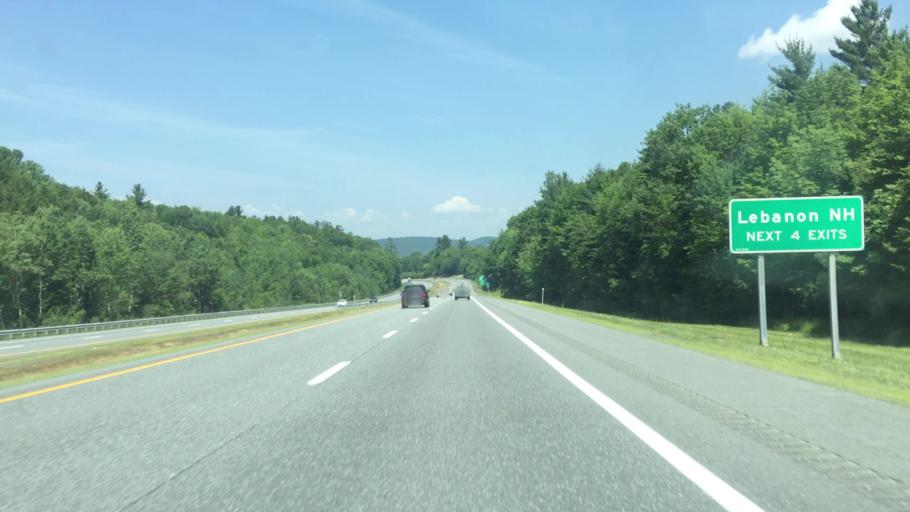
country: US
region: New Hampshire
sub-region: Grafton County
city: Enfield
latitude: 43.6184
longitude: -72.1962
